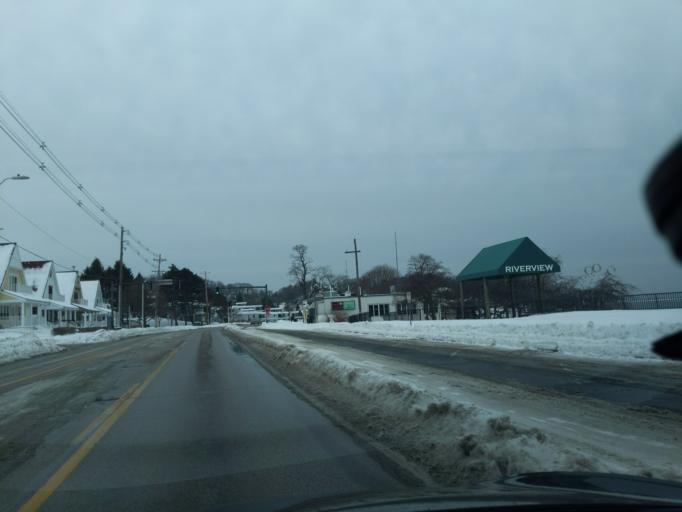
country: US
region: Michigan
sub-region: Ottawa County
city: Grand Haven
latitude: 43.0628
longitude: -86.2354
